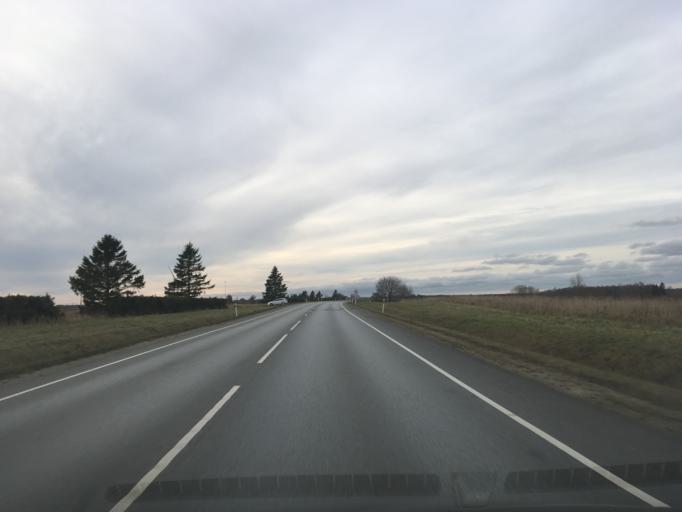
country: EE
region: Ida-Virumaa
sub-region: Aseri vald
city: Aseri
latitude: 59.4405
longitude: 26.8036
